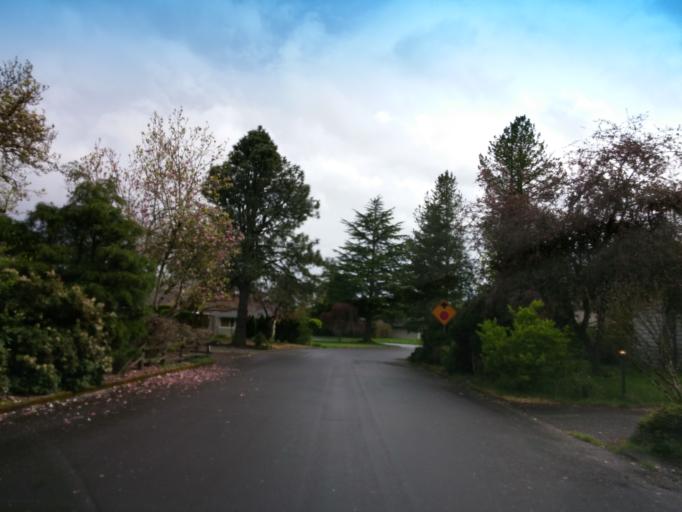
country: US
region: Oregon
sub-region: Washington County
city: Cedar Mill
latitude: 45.5176
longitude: -122.8249
